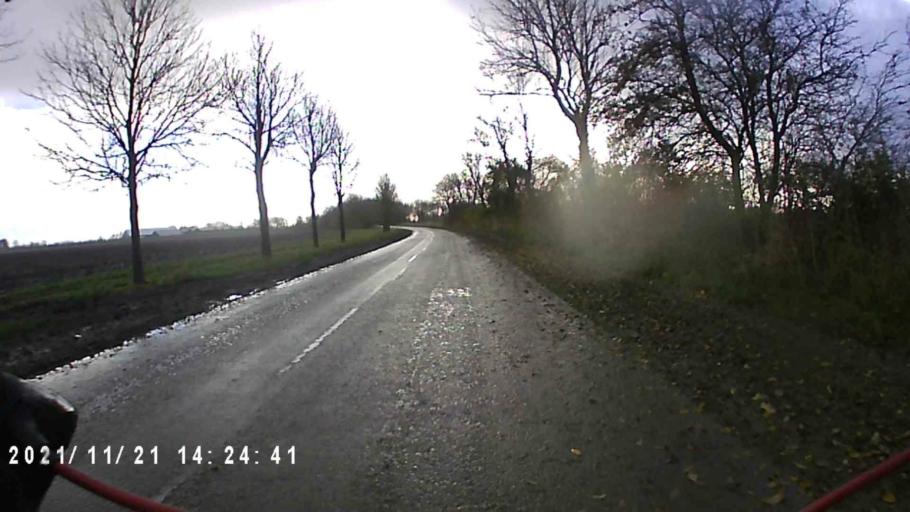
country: NL
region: Groningen
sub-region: Gemeente De Marne
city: Ulrum
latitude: 53.3697
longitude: 6.2909
